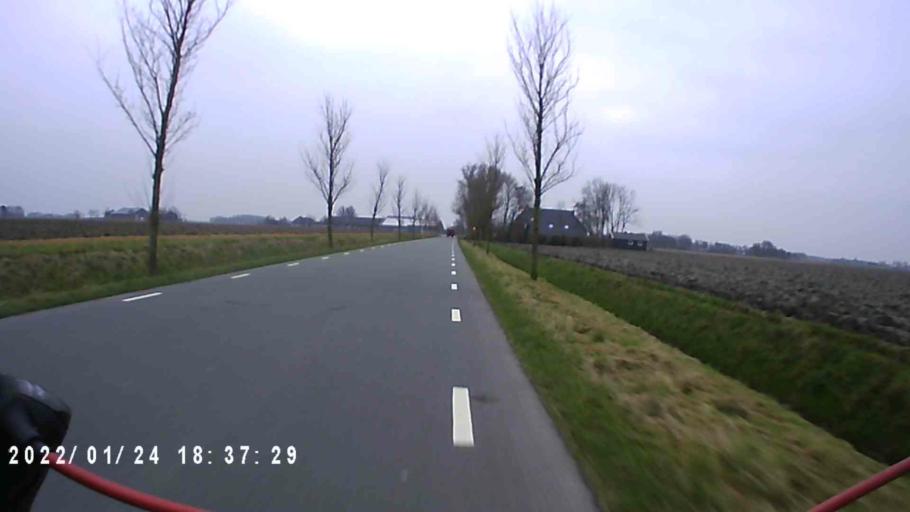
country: NL
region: Groningen
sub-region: Gemeente De Marne
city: Ulrum
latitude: 53.3515
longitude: 6.3361
